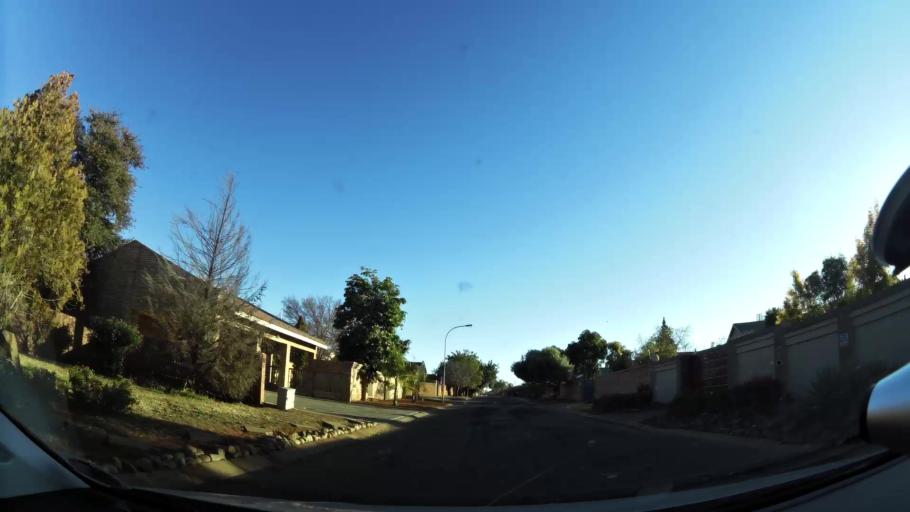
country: ZA
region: Northern Cape
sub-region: Frances Baard District Municipality
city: Kimberley
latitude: -28.7580
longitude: 24.7559
